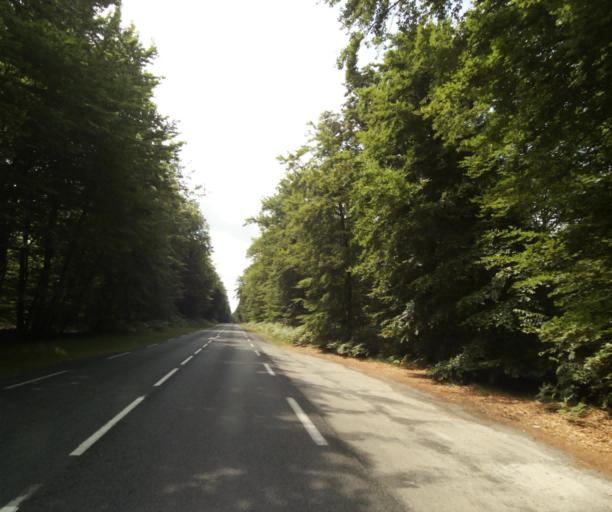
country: FR
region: Ile-de-France
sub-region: Departement de Seine-et-Marne
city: Fontainebleau
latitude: 48.4120
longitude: 2.6548
